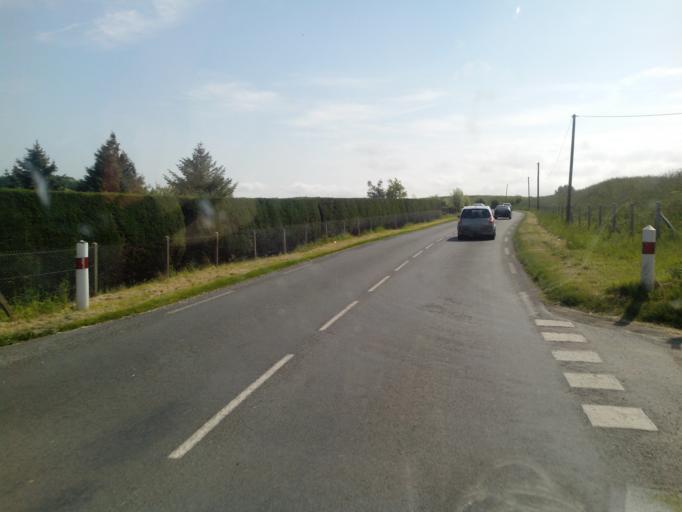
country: FR
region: Picardie
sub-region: Departement de la Somme
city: Quend
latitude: 50.3300
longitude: 1.6430
